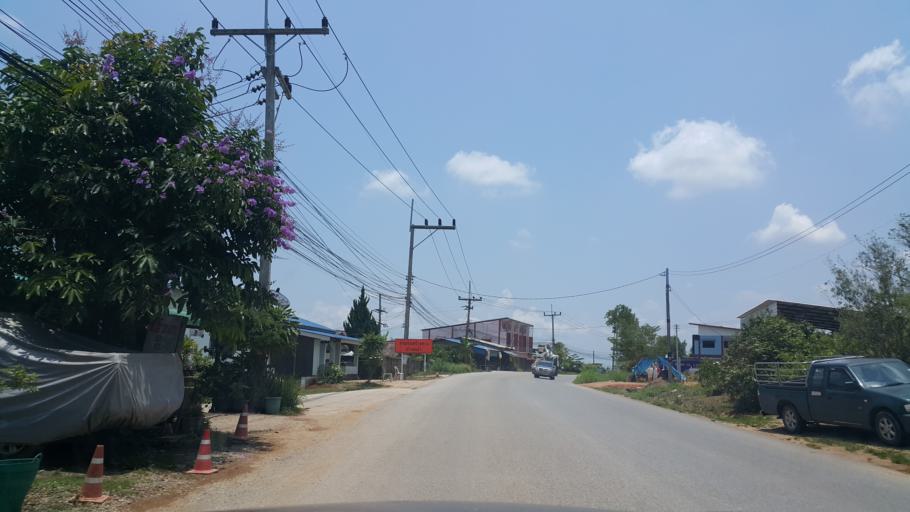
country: TH
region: Chiang Rai
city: Chiang Rai
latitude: 19.9428
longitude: 99.8032
